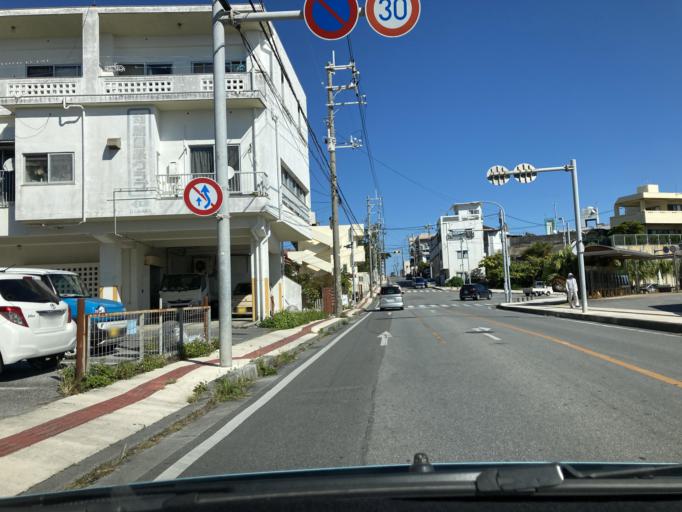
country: JP
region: Okinawa
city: Okinawa
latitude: 26.3286
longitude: 127.8031
